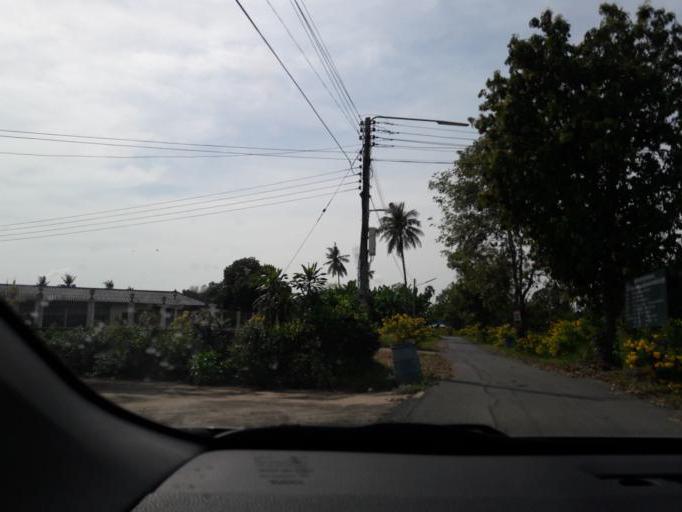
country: TH
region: Ang Thong
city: Ang Thong
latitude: 14.5880
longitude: 100.4400
